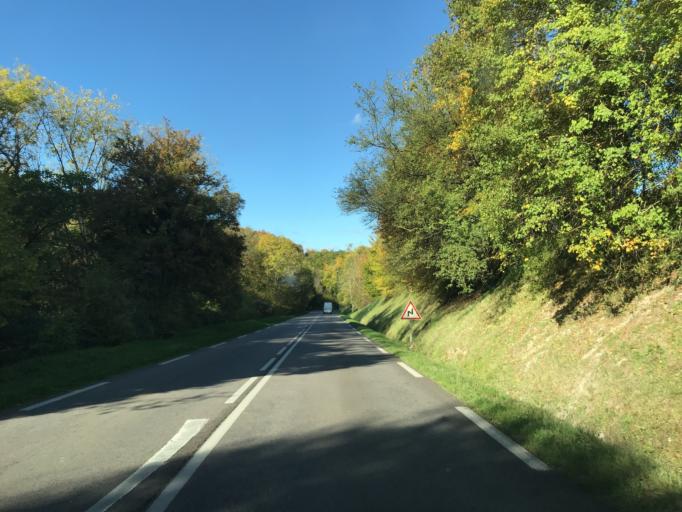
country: FR
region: Haute-Normandie
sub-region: Departement de l'Eure
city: Saint-Aubin-sur-Gaillon
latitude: 49.0831
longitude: 1.2635
